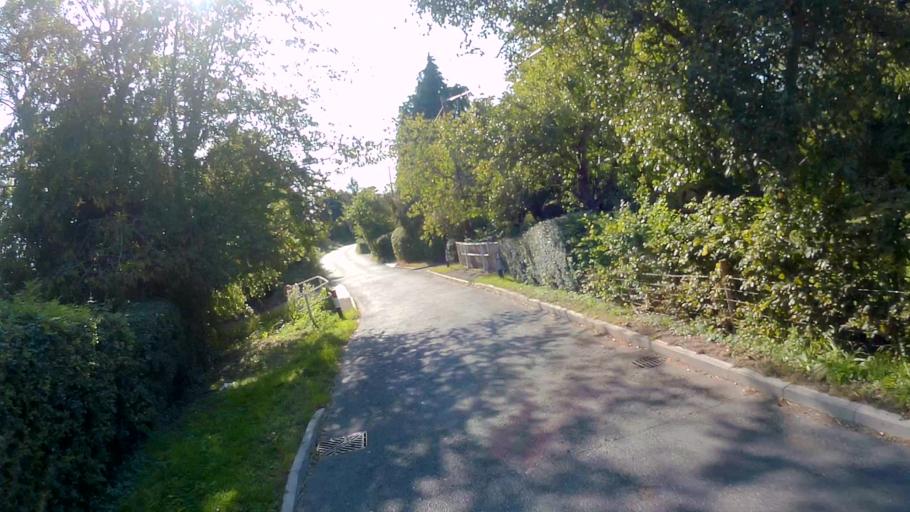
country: GB
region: England
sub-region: Hampshire
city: Kingsley
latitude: 51.1668
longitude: -0.8607
